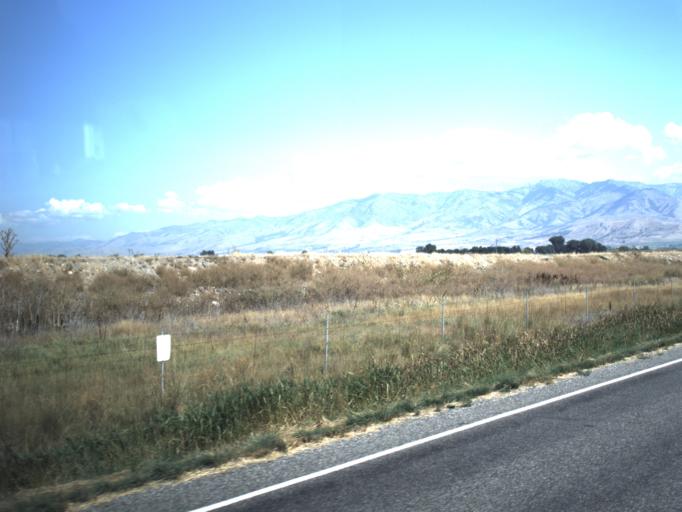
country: US
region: Utah
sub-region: Cache County
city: Benson
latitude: 41.8450
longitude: -111.9116
